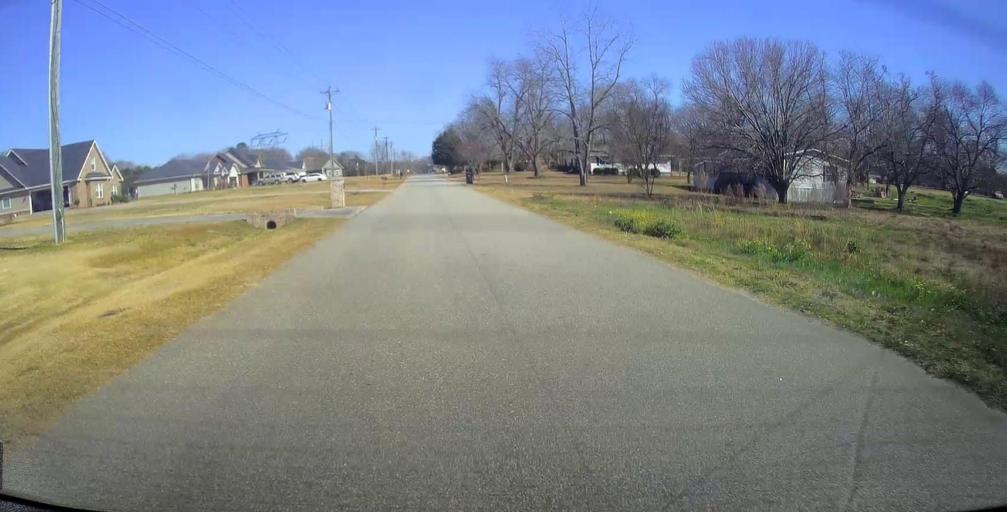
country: US
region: Georgia
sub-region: Peach County
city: Byron
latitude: 32.6356
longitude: -83.7607
